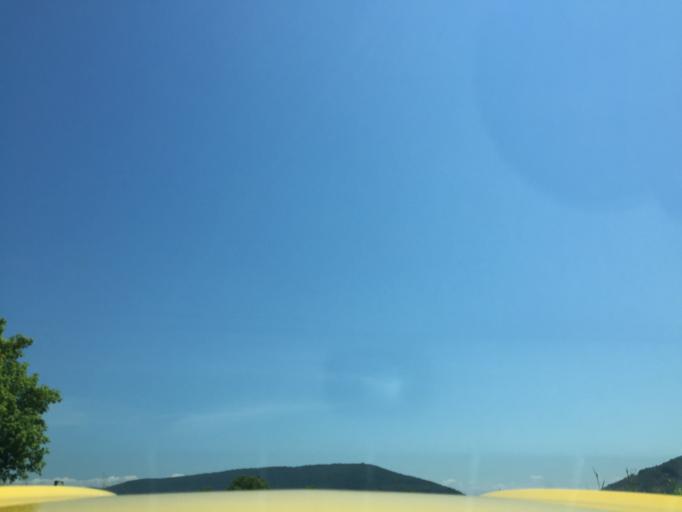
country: US
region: West Virginia
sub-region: Jefferson County
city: Bolivar
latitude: 39.3190
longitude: -77.7614
